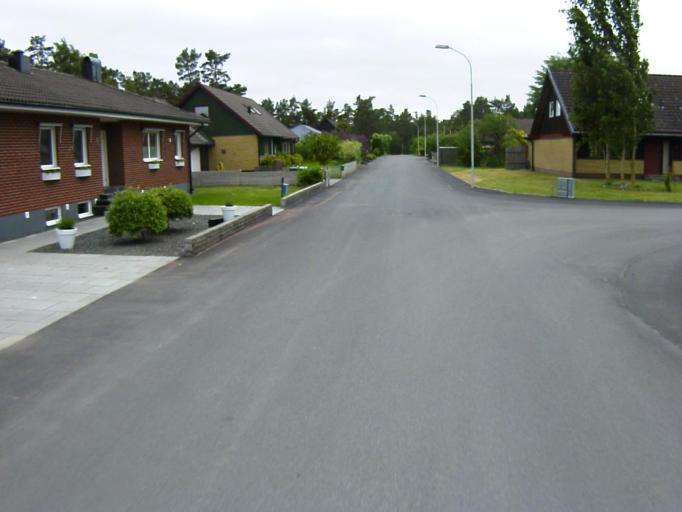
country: SE
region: Skane
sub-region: Kristianstads Kommun
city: Ahus
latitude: 55.9440
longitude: 14.2924
